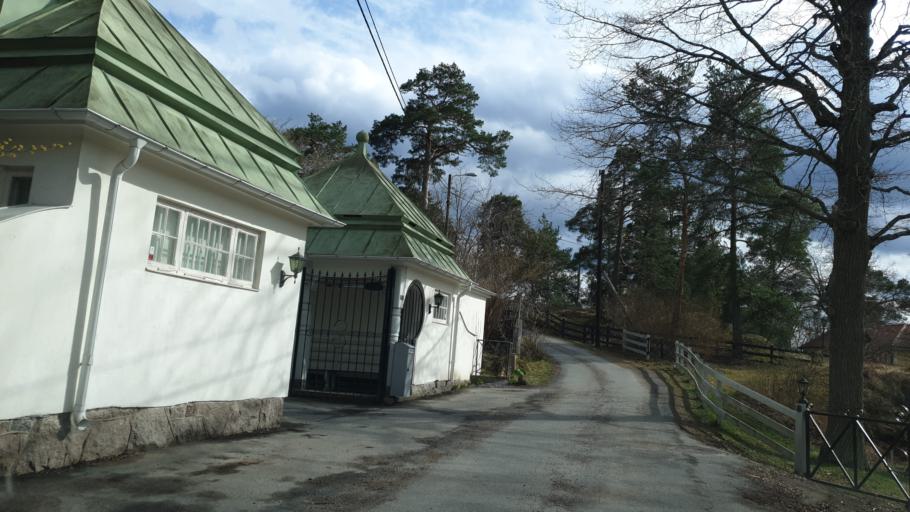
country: SE
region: Stockholm
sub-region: Nacka Kommun
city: Saltsjobaden
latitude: 59.2685
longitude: 18.3122
